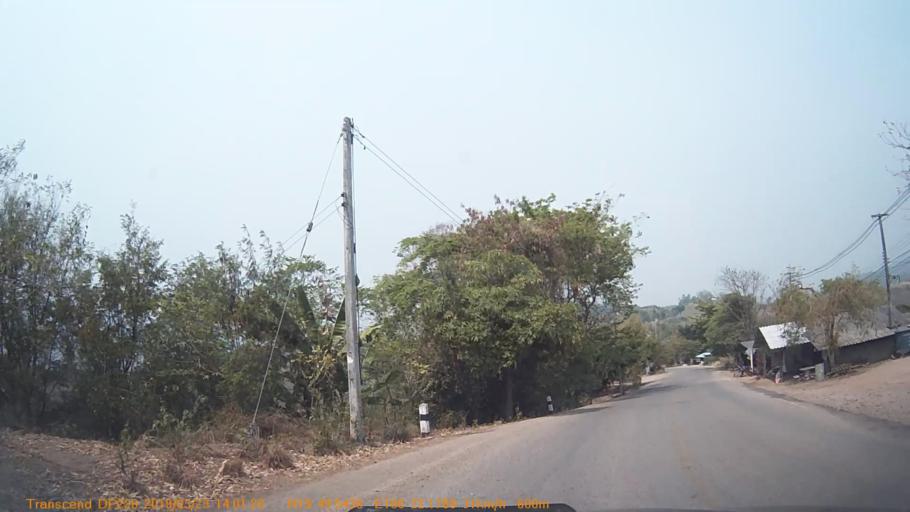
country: TH
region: Chiang Rai
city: Khun Tan
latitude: 19.8258
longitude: 100.3697
